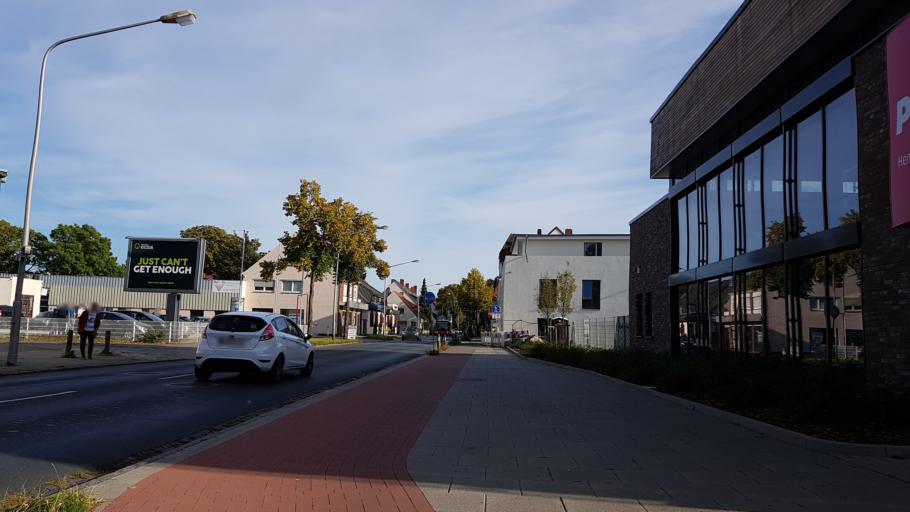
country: DE
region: Lower Saxony
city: Lilienthal
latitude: 53.0473
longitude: 8.8935
